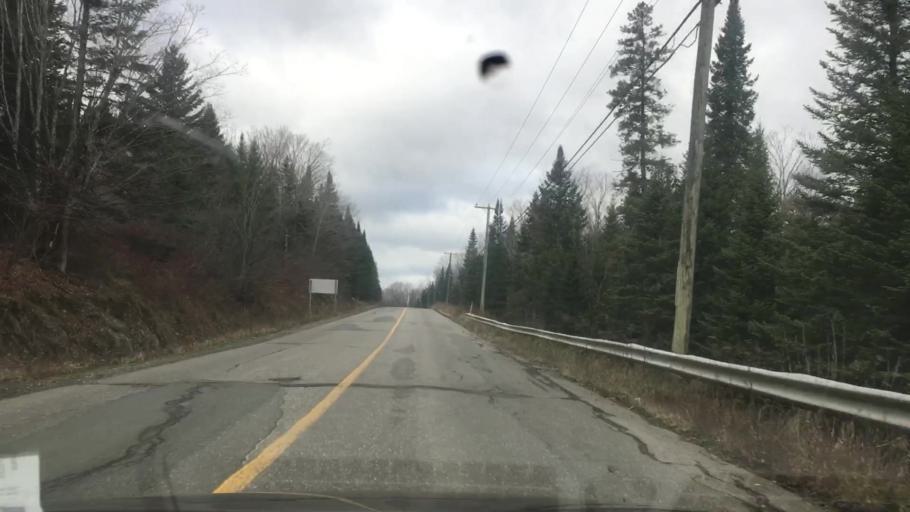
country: US
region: Maine
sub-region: Aroostook County
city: Fort Fairfield
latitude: 46.7505
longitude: -67.7233
